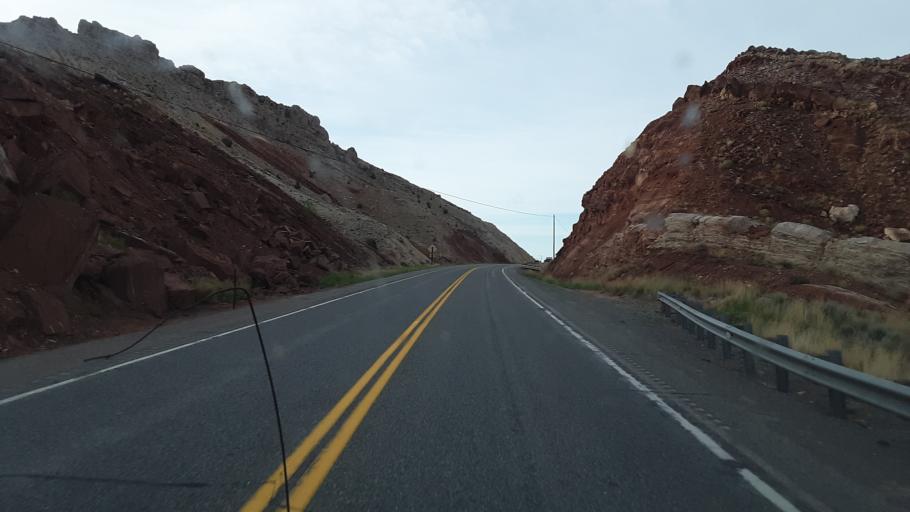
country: US
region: Wyoming
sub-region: Hot Springs County
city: Thermopolis
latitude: 43.4016
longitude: -108.1662
